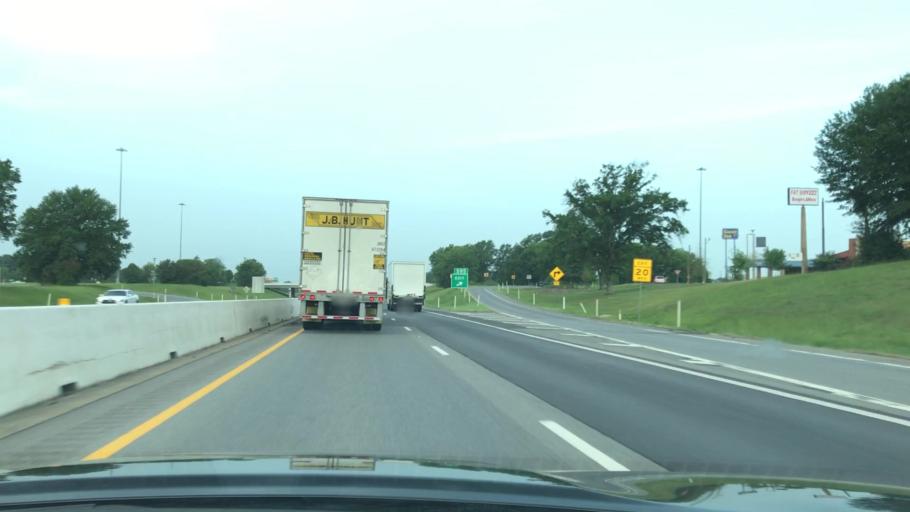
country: US
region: Texas
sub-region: Gregg County
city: Longview
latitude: 32.4474
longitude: -94.7169
